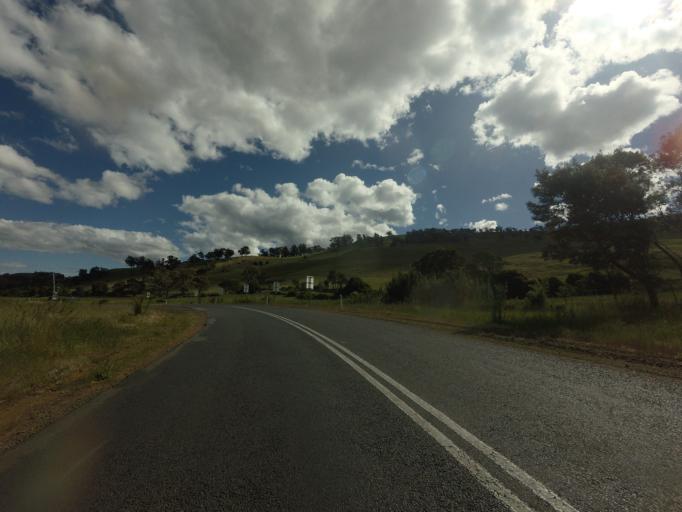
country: AU
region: Tasmania
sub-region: Brighton
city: Bridgewater
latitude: -42.5070
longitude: 147.3492
